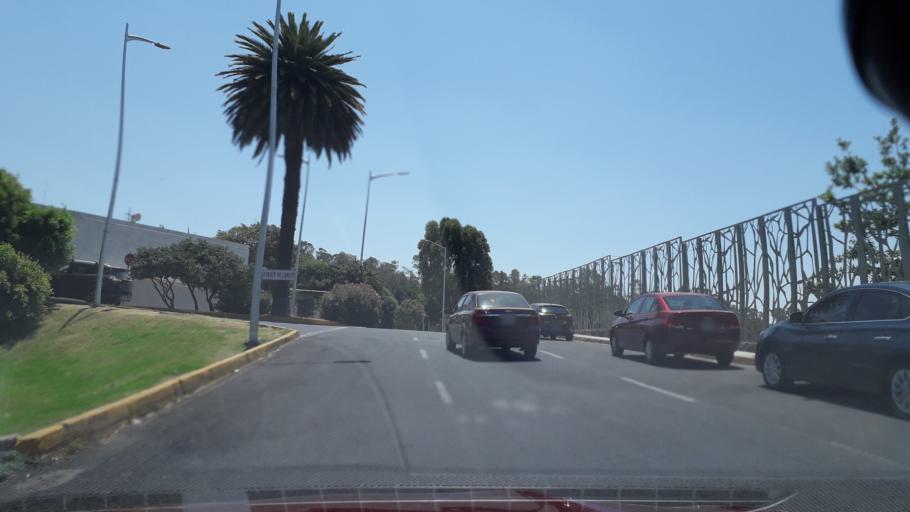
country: MX
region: Puebla
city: Puebla
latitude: 19.0564
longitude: -98.1868
